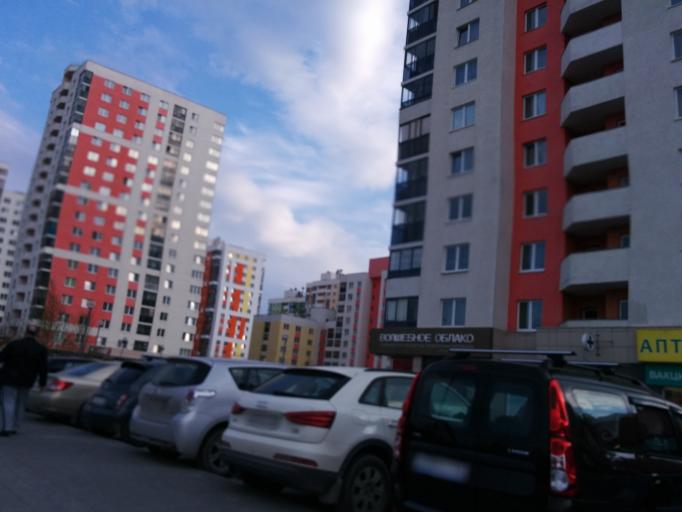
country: RU
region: Sverdlovsk
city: Sovkhoznyy
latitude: 56.7910
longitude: 60.5249
